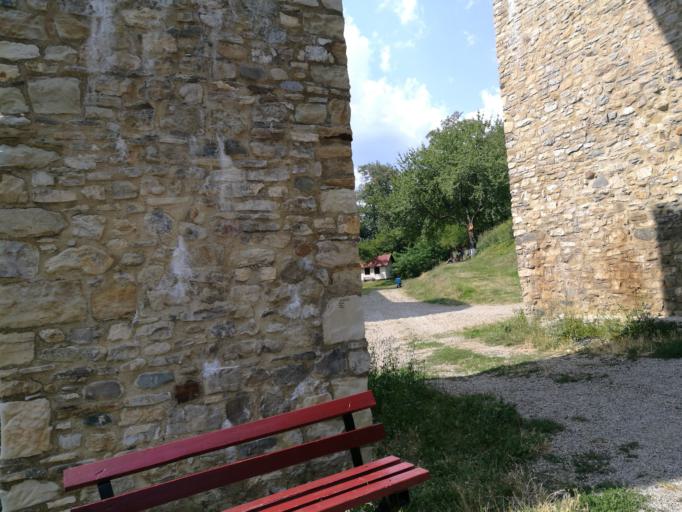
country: RO
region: Neamt
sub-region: Oras Targu Neamt
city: Humulesti
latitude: 47.2148
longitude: 26.3441
